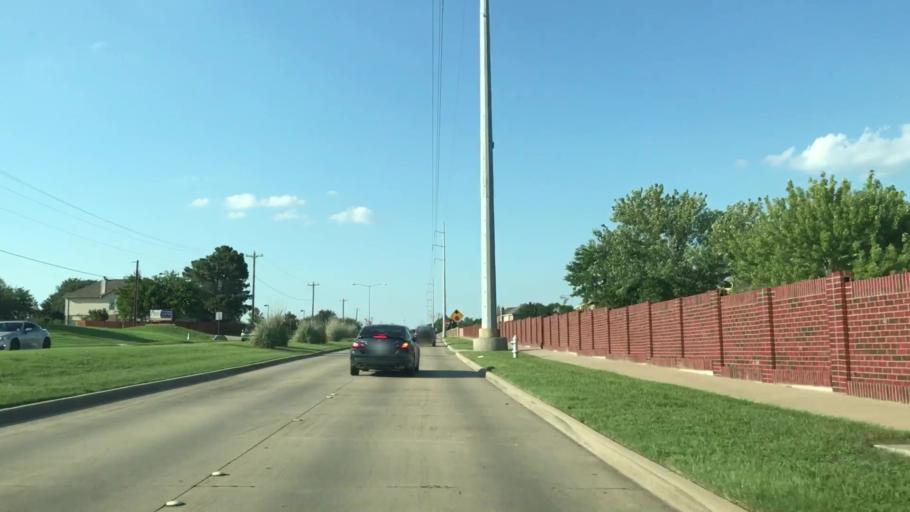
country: US
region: Texas
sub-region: Denton County
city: Lewisville
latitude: 33.0340
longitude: -97.0360
